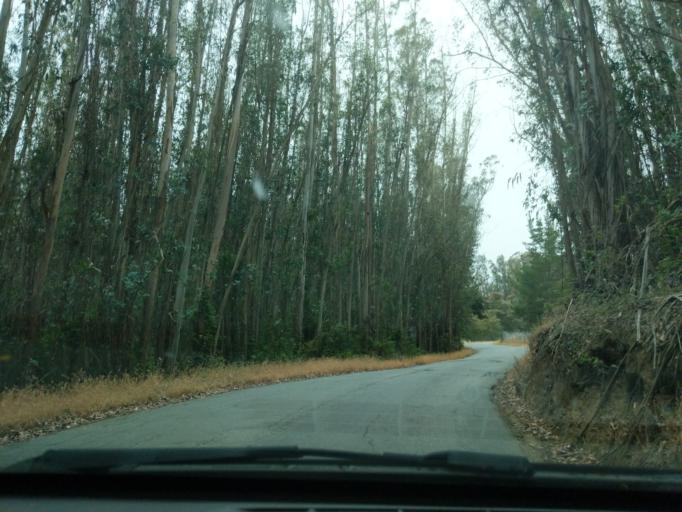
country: US
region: California
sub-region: San Benito County
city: Aromas
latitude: 36.8903
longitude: -121.6075
